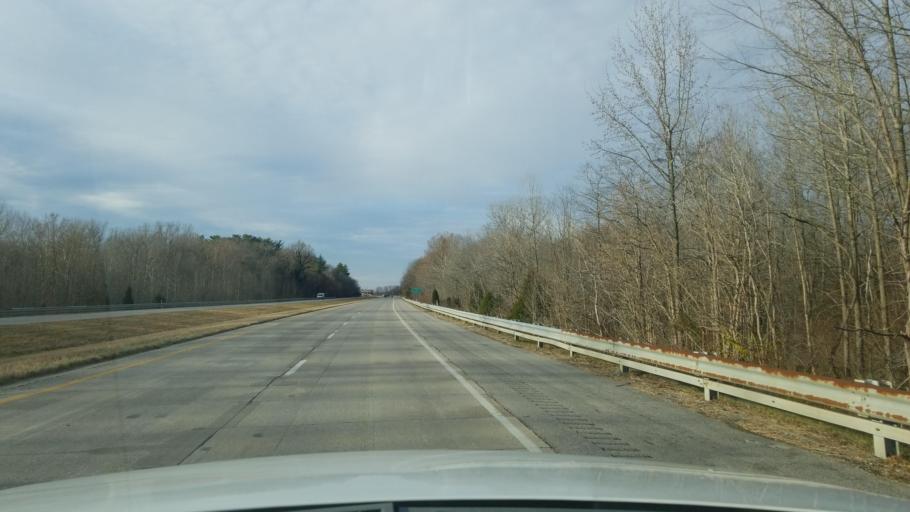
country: US
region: Indiana
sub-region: Vanderburgh County
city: Evansville
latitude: 37.9470
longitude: -87.7071
